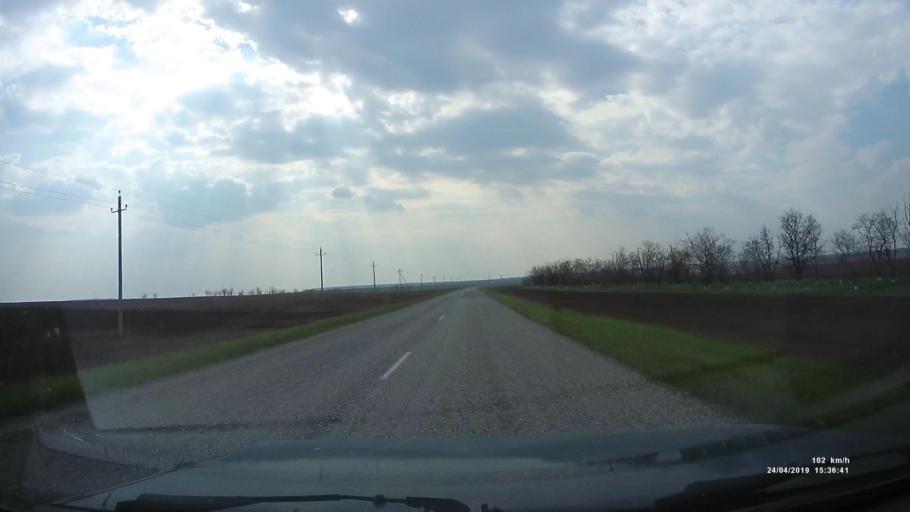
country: RU
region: Kalmykiya
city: Yashalta
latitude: 46.5995
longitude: 42.8655
